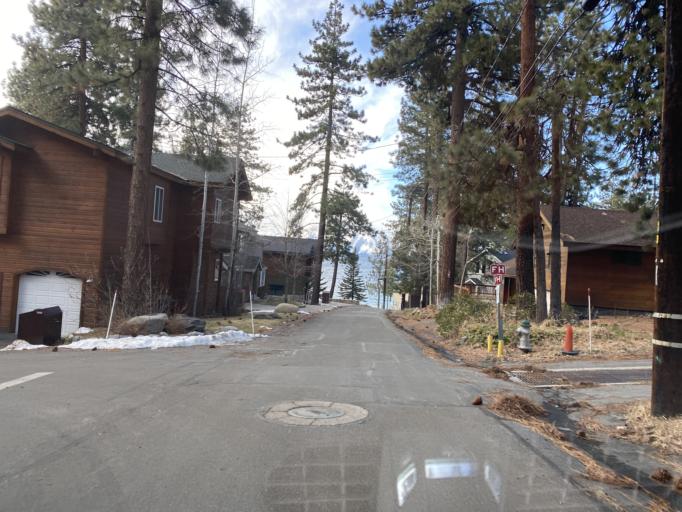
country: US
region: Nevada
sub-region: Douglas County
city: Kingsbury
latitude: 39.0005
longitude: -119.9574
